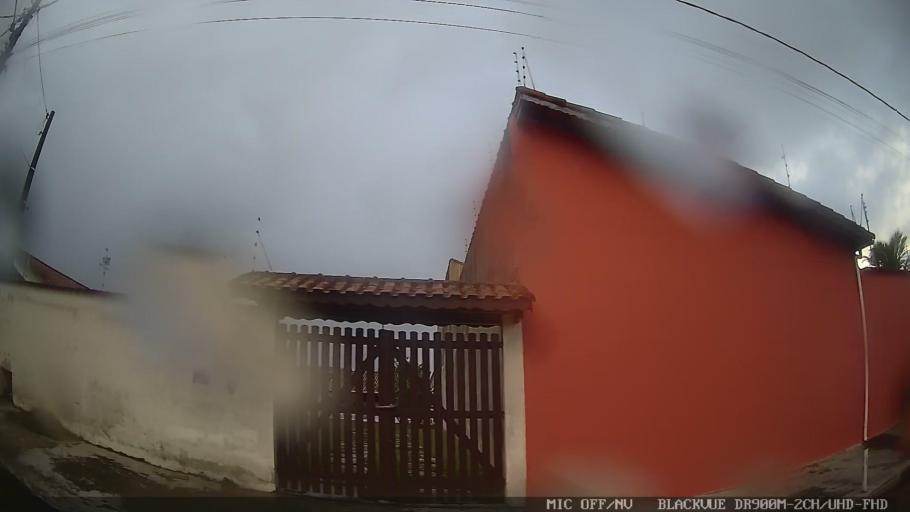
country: BR
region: Sao Paulo
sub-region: Itanhaem
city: Itanhaem
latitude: -24.2089
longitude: -46.8419
